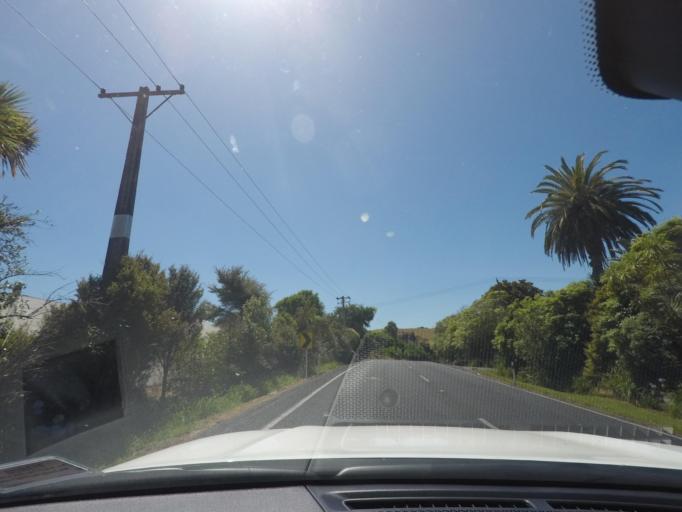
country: NZ
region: Auckland
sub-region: Auckland
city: Parakai
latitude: -36.6090
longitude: 174.3349
